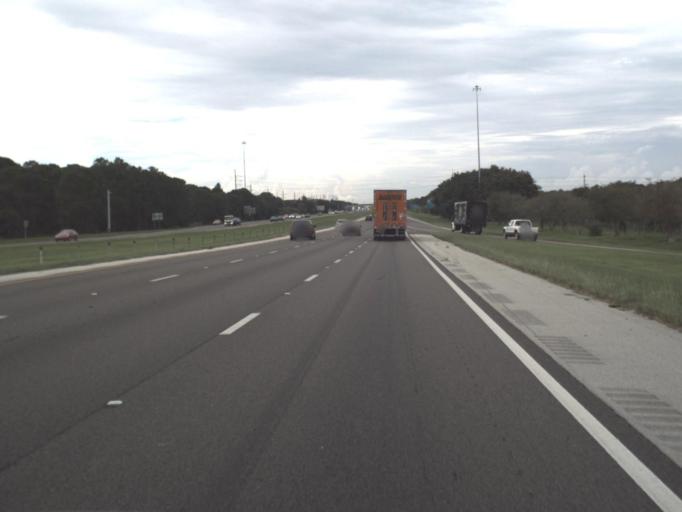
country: US
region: Florida
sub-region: Sarasota County
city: Lake Sarasota
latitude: 27.2963
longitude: -82.4483
